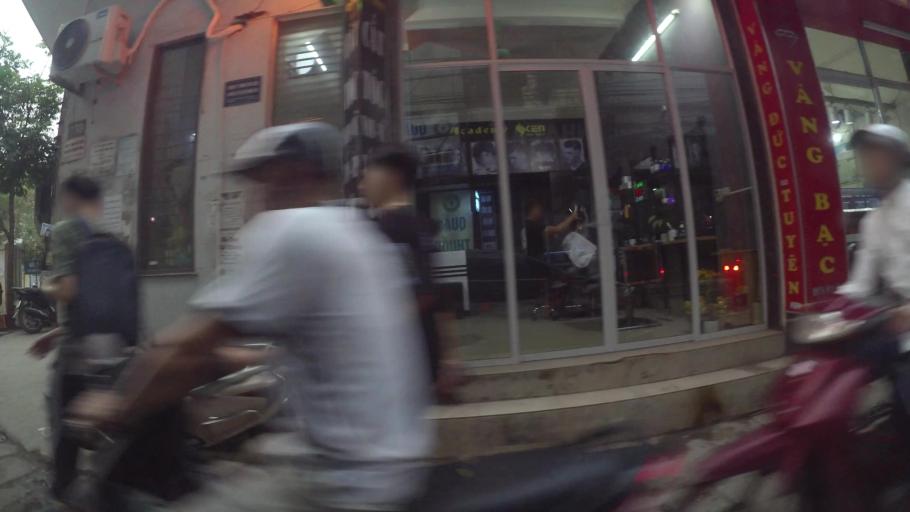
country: VN
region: Ha Noi
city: Thanh Xuan
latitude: 20.9817
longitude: 105.8007
